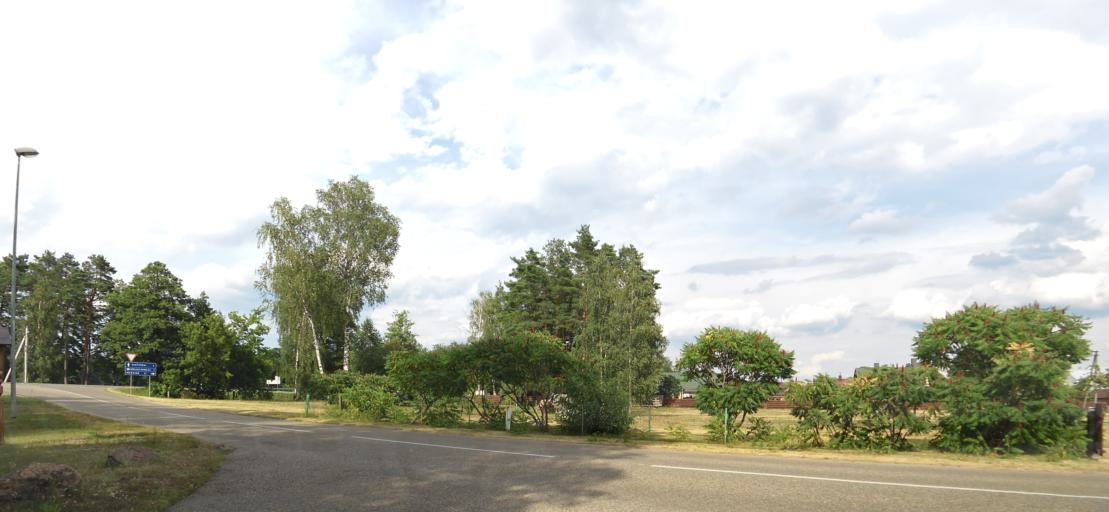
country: LT
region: Alytaus apskritis
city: Druskininkai
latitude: 54.0324
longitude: 24.0748
